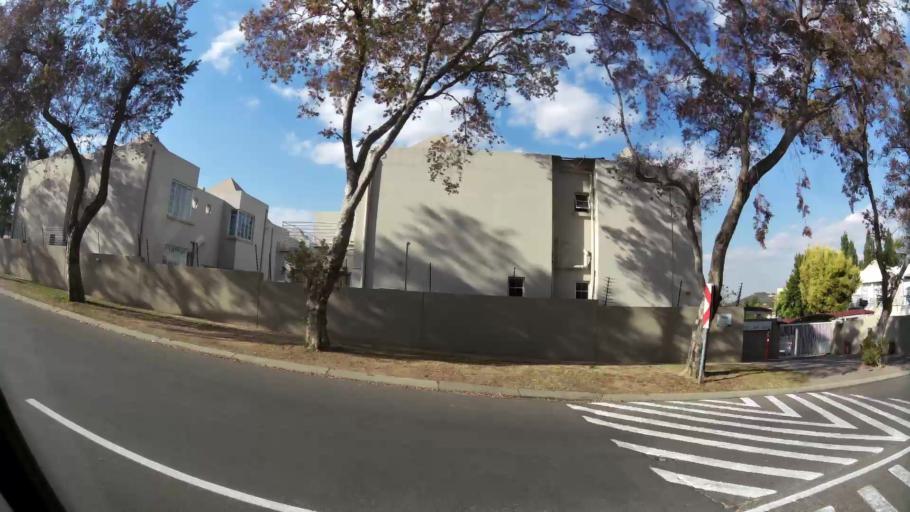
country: ZA
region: Gauteng
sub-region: City of Johannesburg Metropolitan Municipality
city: Diepsloot
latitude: -26.0113
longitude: 28.0302
